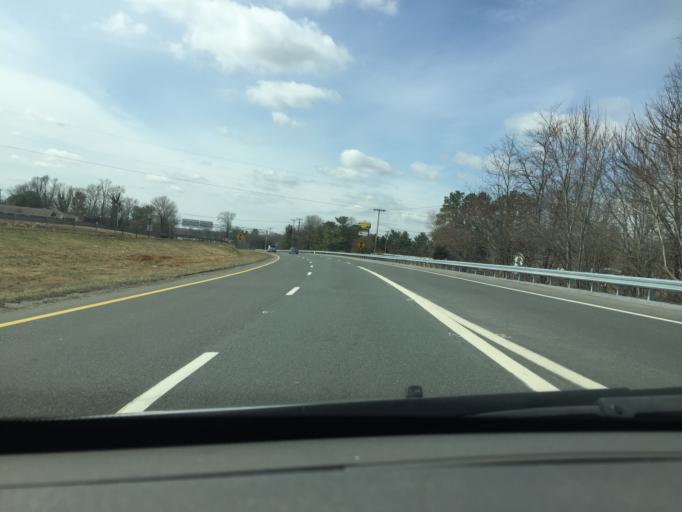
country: US
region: Virginia
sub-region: Campbell County
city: Timberlake
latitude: 37.3094
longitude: -79.2662
